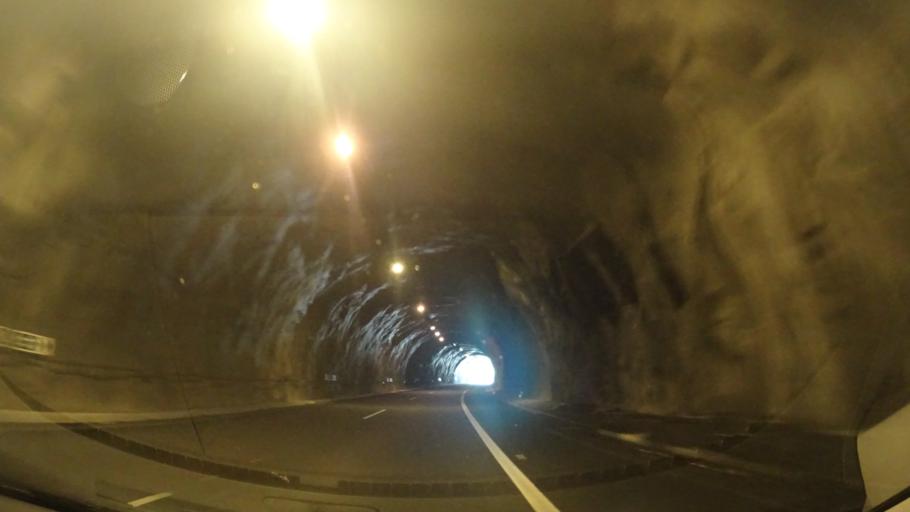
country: ES
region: Asturias
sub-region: Province of Asturias
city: Mieres
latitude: 43.2868
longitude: -5.7577
